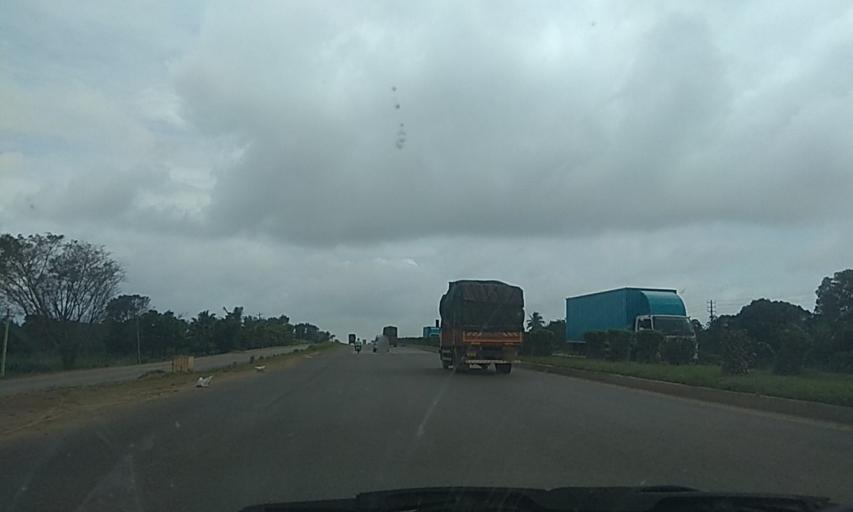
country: IN
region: Karnataka
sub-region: Dharwad
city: Kundgol
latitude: 15.1726
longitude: 75.1398
